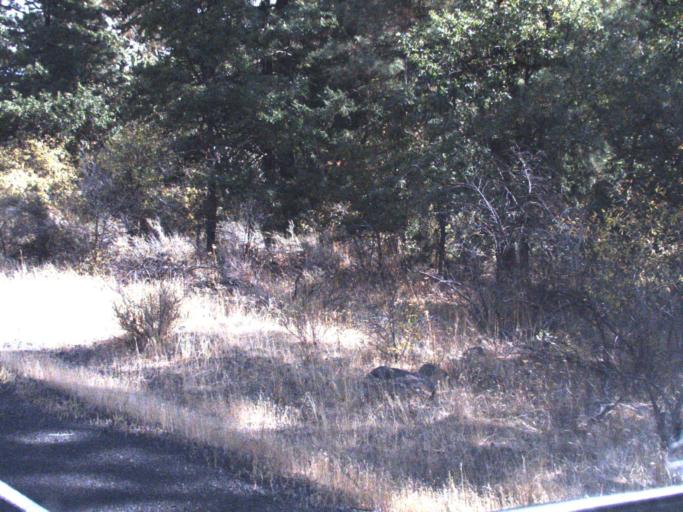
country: US
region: Washington
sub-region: Yakima County
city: Tieton
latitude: 46.7072
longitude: -120.8884
